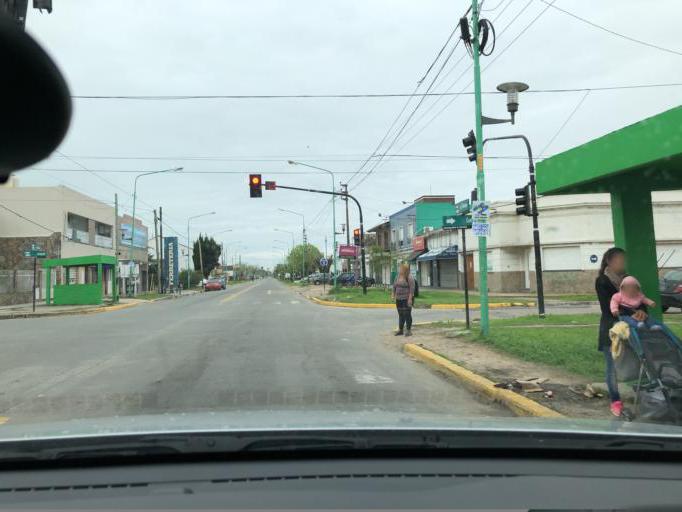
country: AR
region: Buenos Aires
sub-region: Partido de Ensenada
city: Ensenada
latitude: -34.8558
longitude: -57.9185
